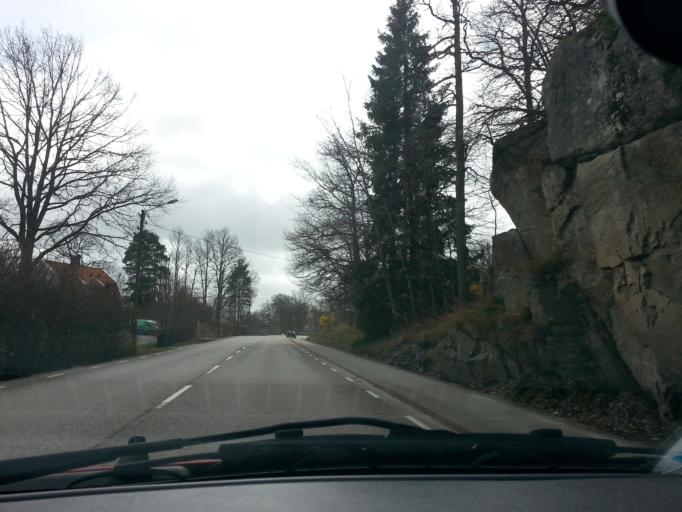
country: SE
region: Vaestra Goetaland
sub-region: Lerums Kommun
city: Grabo
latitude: 57.8723
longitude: 12.3264
